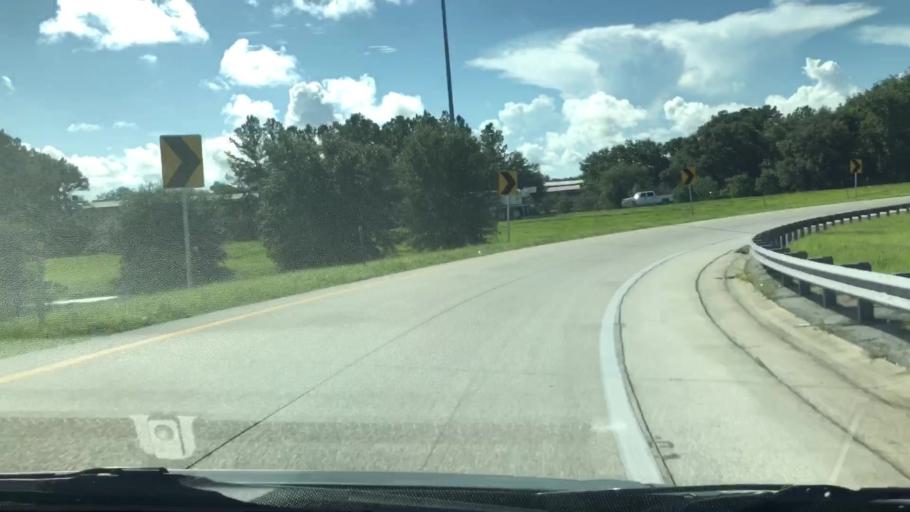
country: US
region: Florida
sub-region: Saint Johns County
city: Fruit Cove
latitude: 30.1674
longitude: -81.5379
